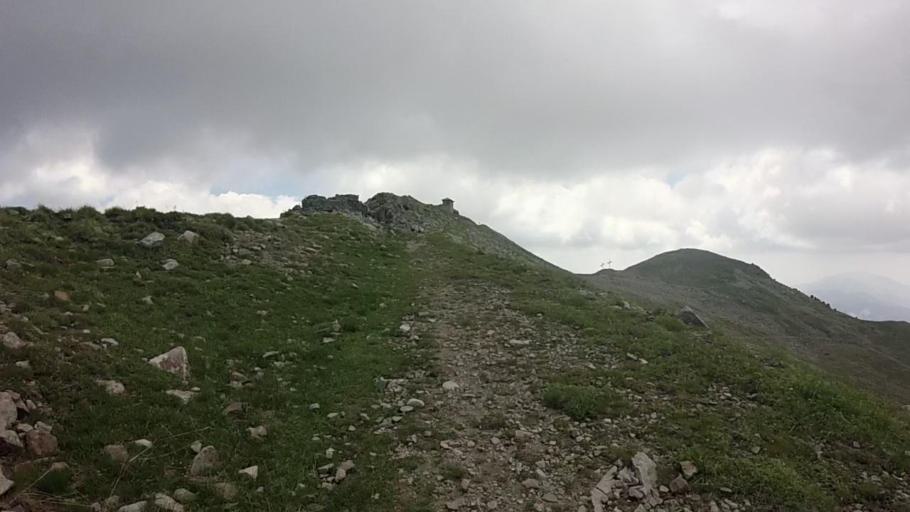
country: FR
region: Provence-Alpes-Cote d'Azur
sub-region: Departement des Alpes-de-Haute-Provence
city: Seyne-les-Alpes
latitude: 44.4111
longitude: 6.3847
